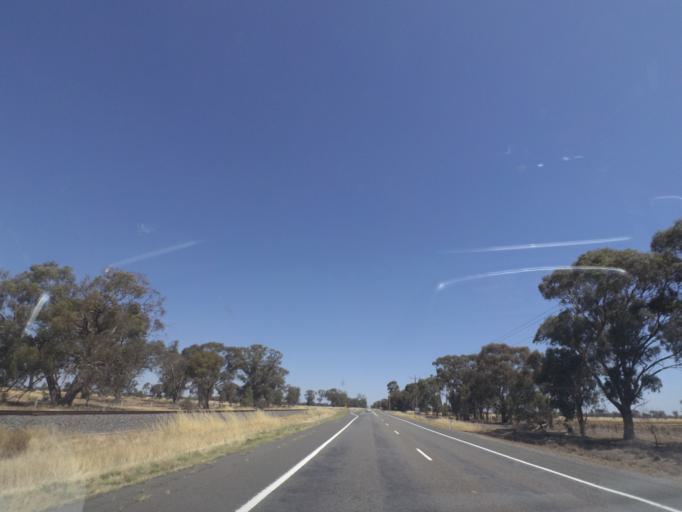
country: AU
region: Victoria
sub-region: Greater Shepparton
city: Shepparton
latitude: -36.1975
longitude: 145.4318
